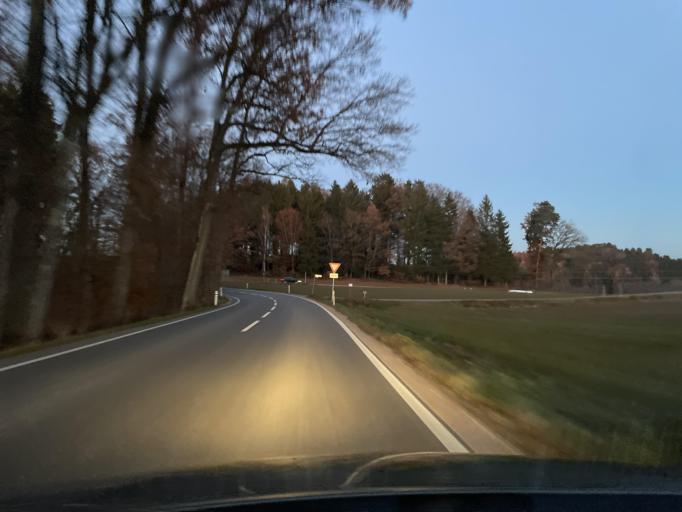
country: DE
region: Bavaria
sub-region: Lower Bavaria
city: Reut
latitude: 48.3123
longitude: 12.9517
